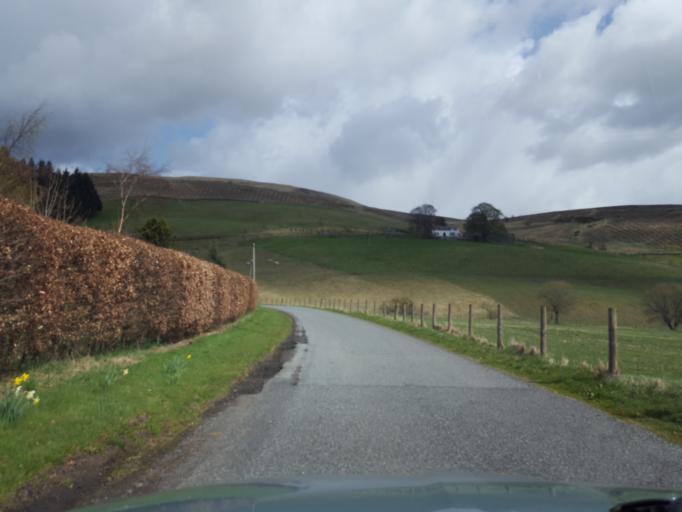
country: GB
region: Scotland
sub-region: Clackmannanshire
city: Dollar
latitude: 56.2289
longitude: -3.5946
